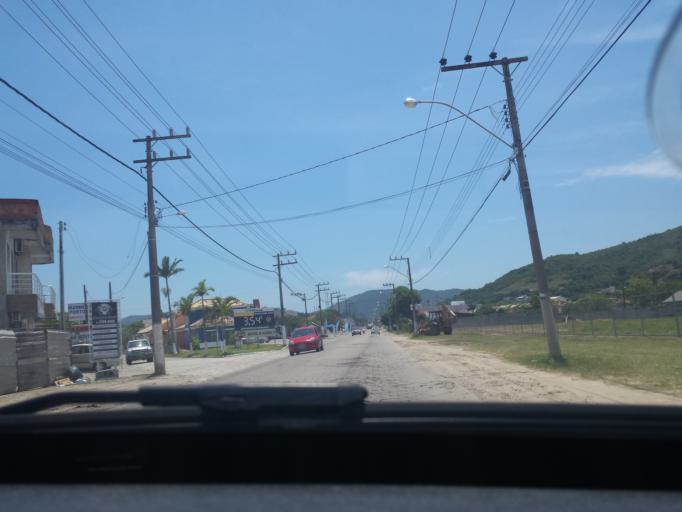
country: BR
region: Santa Catarina
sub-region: Porto Belo
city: Porto Belo
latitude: -27.1594
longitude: -48.5691
